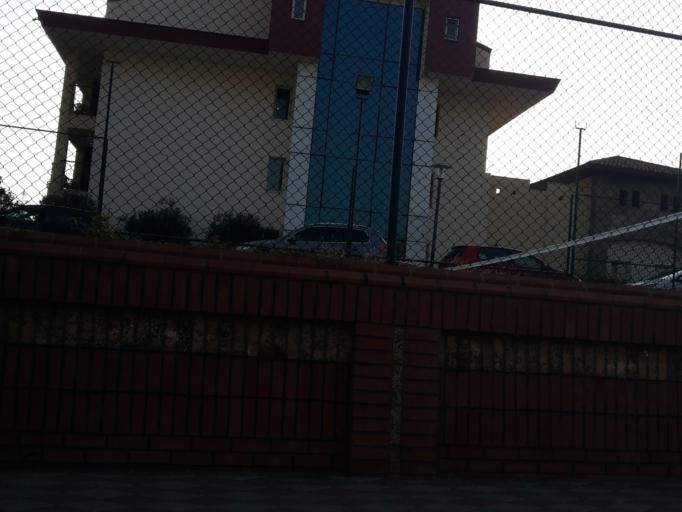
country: TR
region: Antalya
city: Kemer
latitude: 36.6122
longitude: 30.5571
